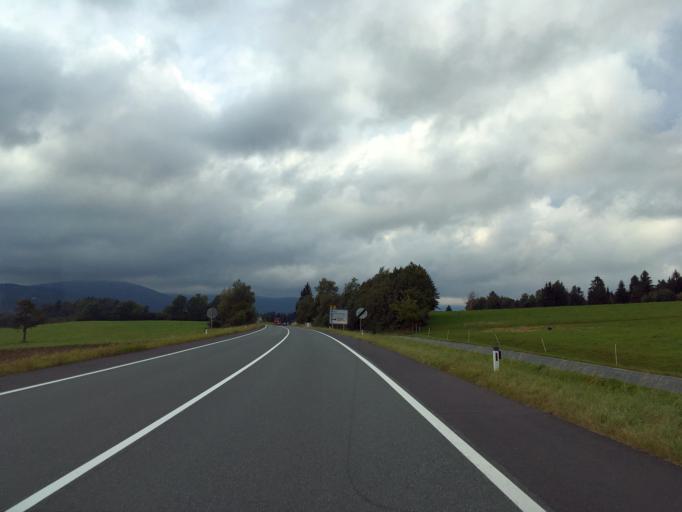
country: AT
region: Styria
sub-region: Politischer Bezirk Hartberg-Fuerstenfeld
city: Pinggau
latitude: 47.4559
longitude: 16.0696
